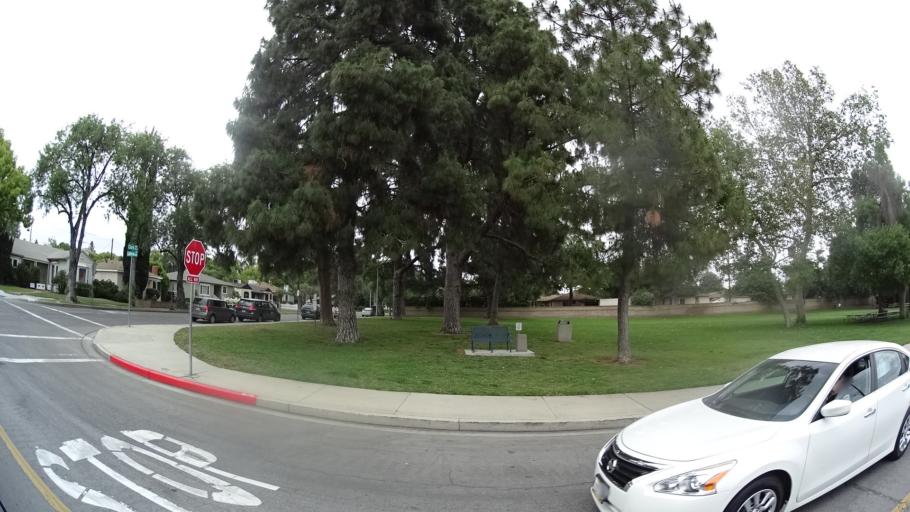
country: US
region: California
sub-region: Los Angeles County
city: Universal City
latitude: 34.1656
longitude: -118.3412
